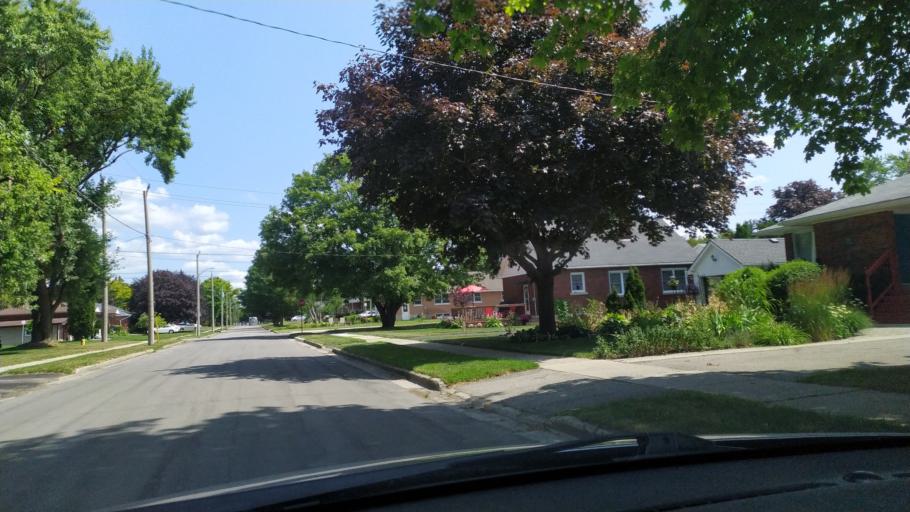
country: CA
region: Ontario
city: Stratford
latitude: 43.3659
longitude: -80.9962
